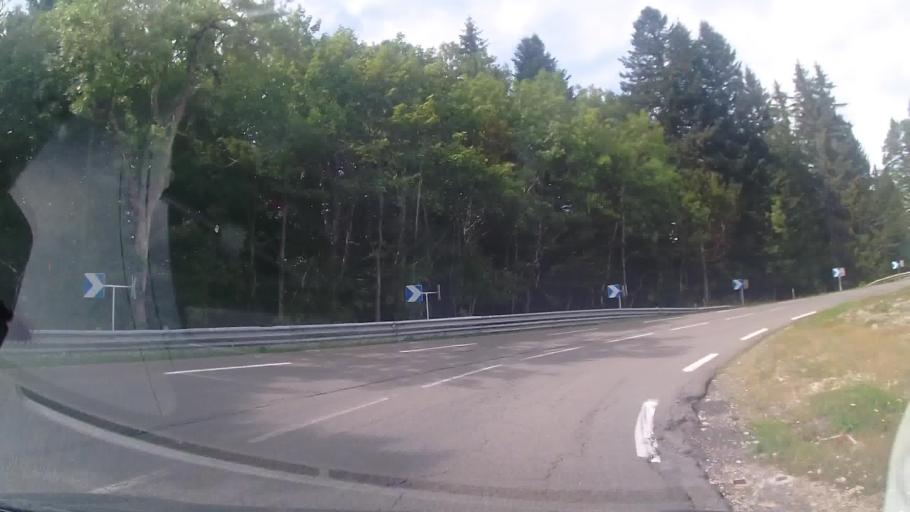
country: FR
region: Franche-Comte
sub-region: Departement du Jura
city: Les Rousses
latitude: 46.4139
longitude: 6.0597
